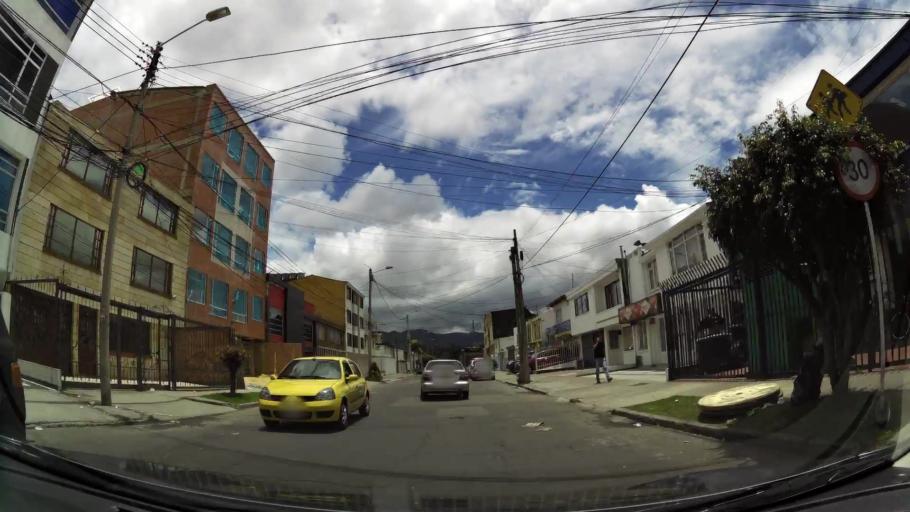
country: CO
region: Bogota D.C.
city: Bogota
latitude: 4.6716
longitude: -74.1041
